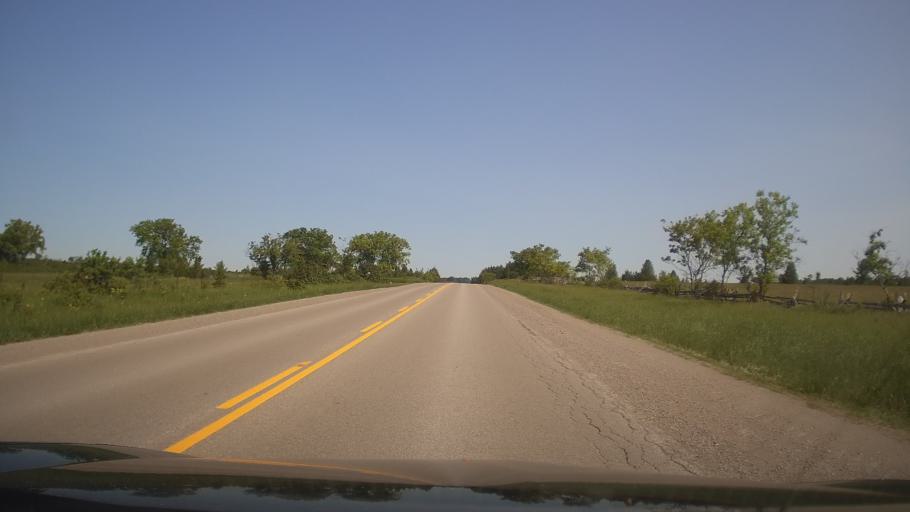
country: CA
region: Ontario
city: Uxbridge
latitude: 44.5108
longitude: -78.9557
